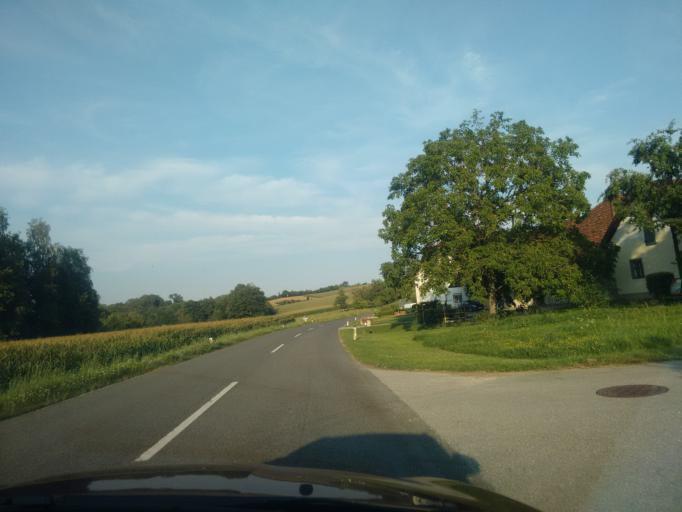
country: AT
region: Upper Austria
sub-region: Wels-Land
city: Bachmanning
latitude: 48.1603
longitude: 13.7833
